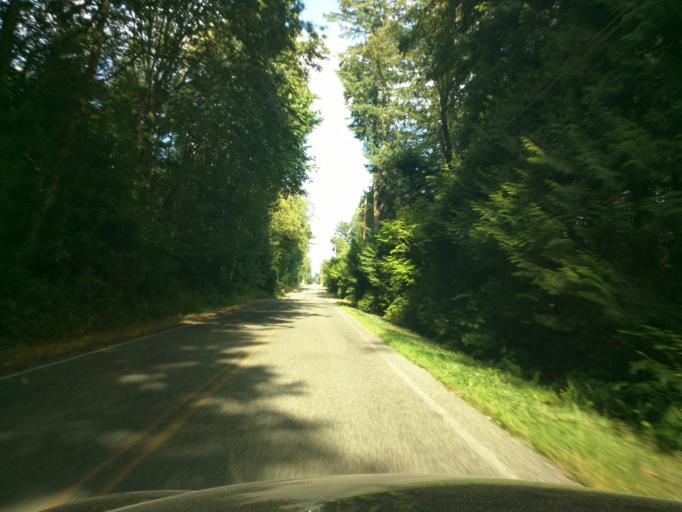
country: US
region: Washington
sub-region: Whatcom County
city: Blaine
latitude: 48.9936
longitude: -122.6658
